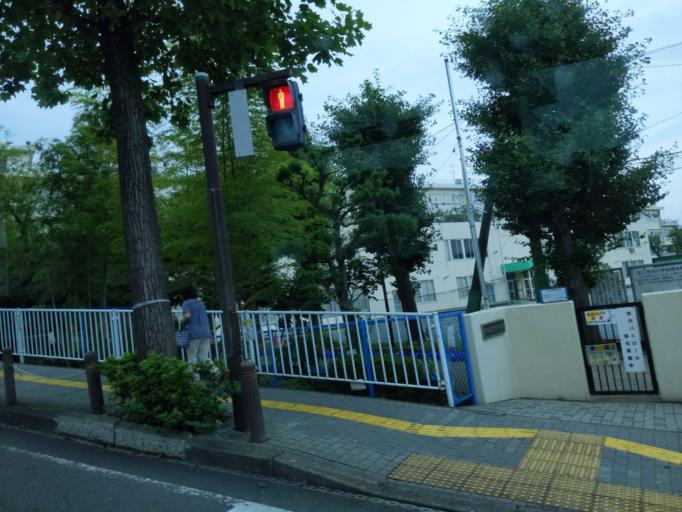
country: JP
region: Tokyo
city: Chofugaoka
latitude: 35.5876
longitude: 139.5792
